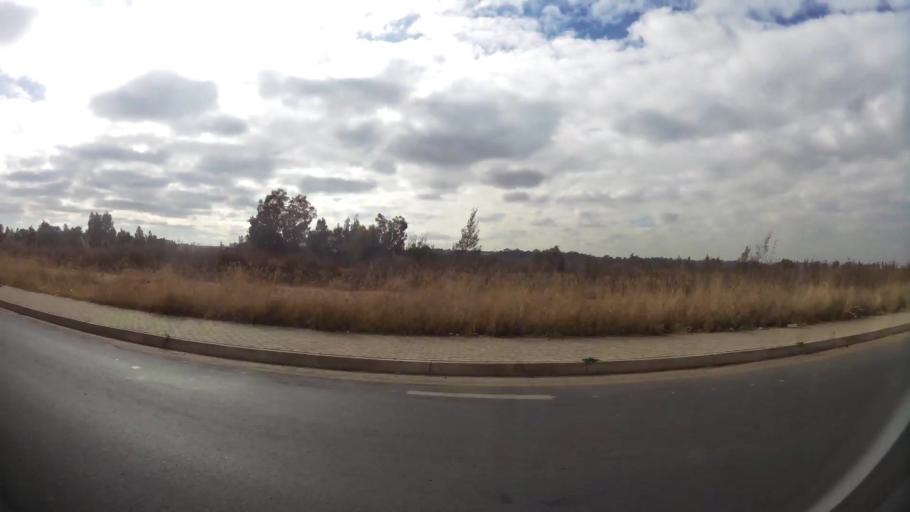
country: ZA
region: Gauteng
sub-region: City of Johannesburg Metropolitan Municipality
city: Roodepoort
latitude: -26.1980
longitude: 27.9027
